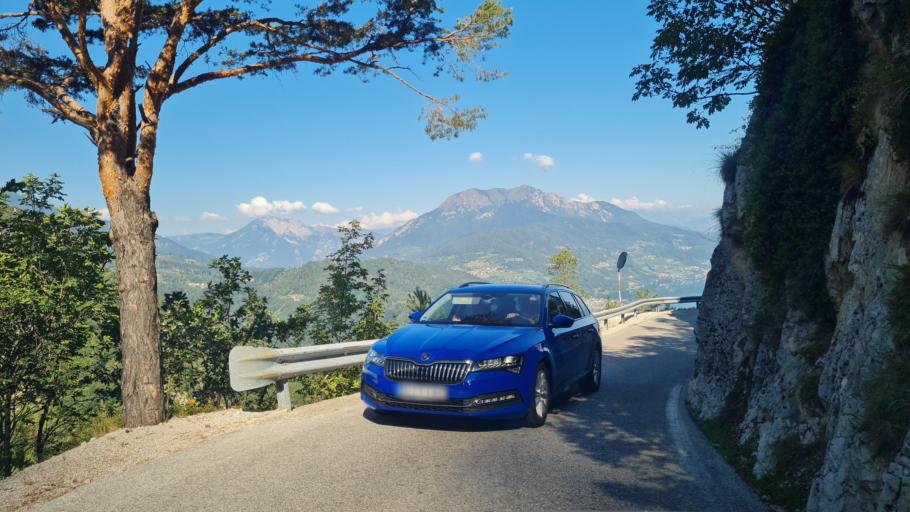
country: IT
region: Trentino-Alto Adige
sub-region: Provincia di Trento
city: Caldonazzo
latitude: 45.9753
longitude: 11.2870
